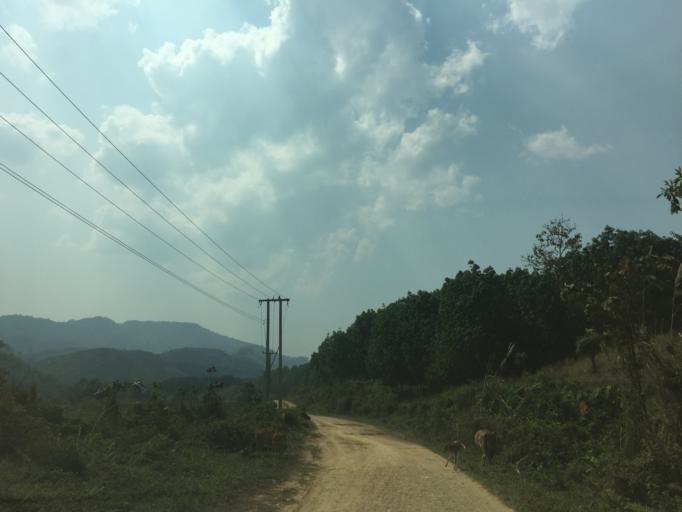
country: TH
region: Nan
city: Thung Chang
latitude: 19.7310
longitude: 100.7399
